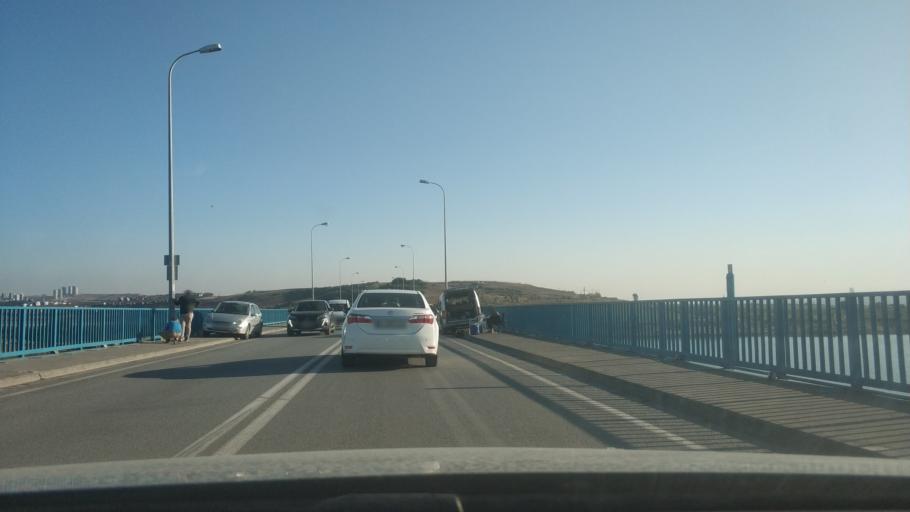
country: TR
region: Adana
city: Adana
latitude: 37.1006
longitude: 35.3025
